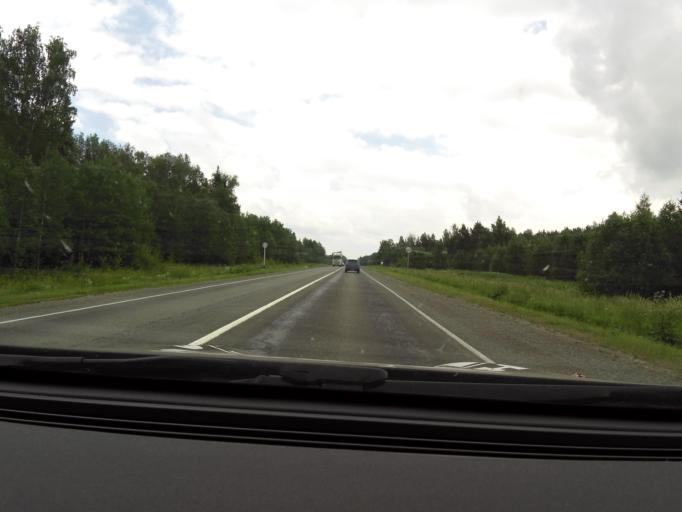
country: RU
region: Perm
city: Suksun
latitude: 56.9215
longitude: 57.5680
